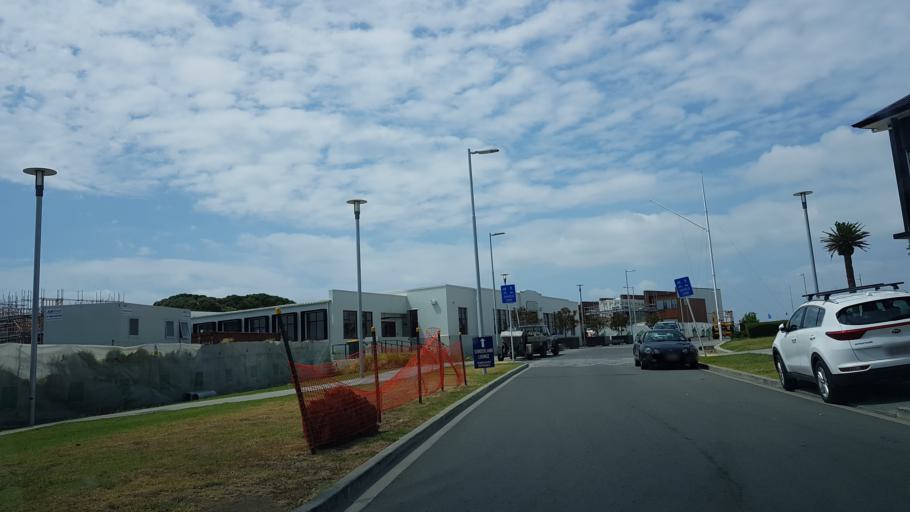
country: NZ
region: Auckland
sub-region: Auckland
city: North Shore
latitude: -36.7876
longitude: 174.6660
